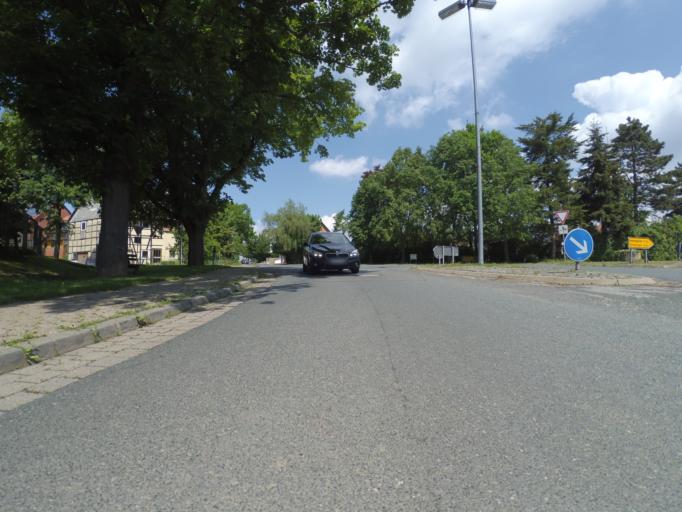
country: DE
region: Lower Saxony
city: Hohenhameln
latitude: 52.2573
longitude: 10.0707
